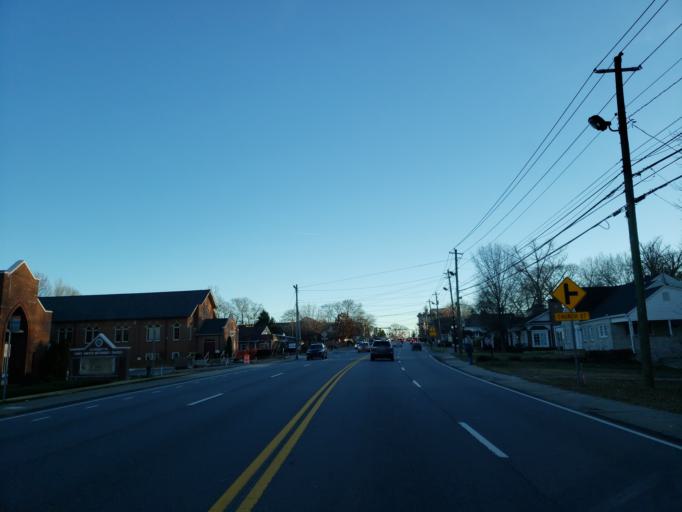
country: US
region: Georgia
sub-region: Fulton County
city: Alpharetta
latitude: 34.0782
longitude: -84.2945
